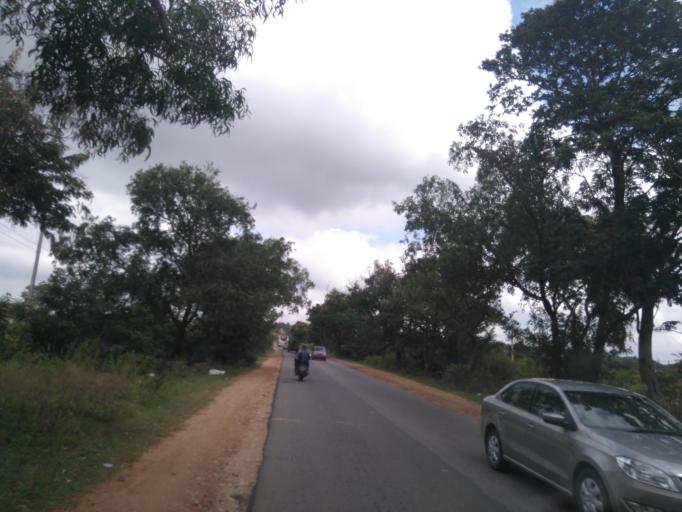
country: IN
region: Karnataka
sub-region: Mysore
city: Mysore
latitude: 12.2844
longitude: 76.7194
